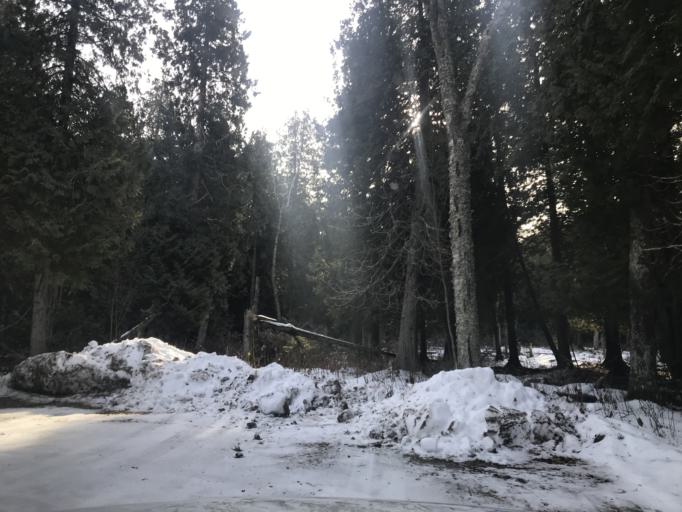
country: US
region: Wisconsin
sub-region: Door County
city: Sturgeon Bay
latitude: 45.1466
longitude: -87.0319
